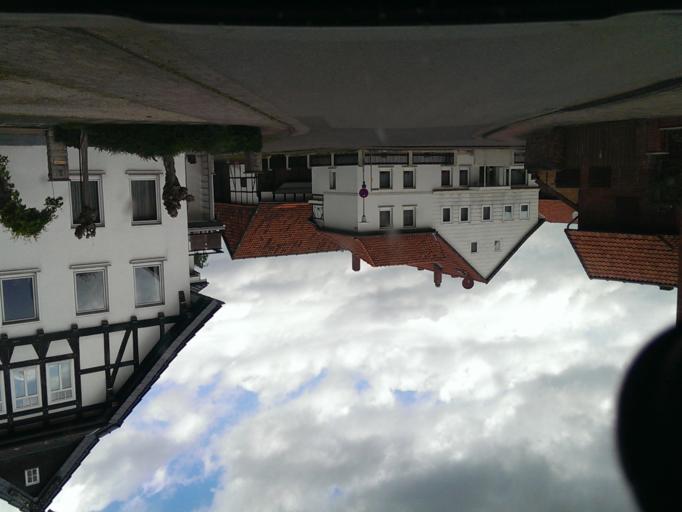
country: DE
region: Lower Saxony
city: Eime
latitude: 52.0782
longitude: 9.7263
